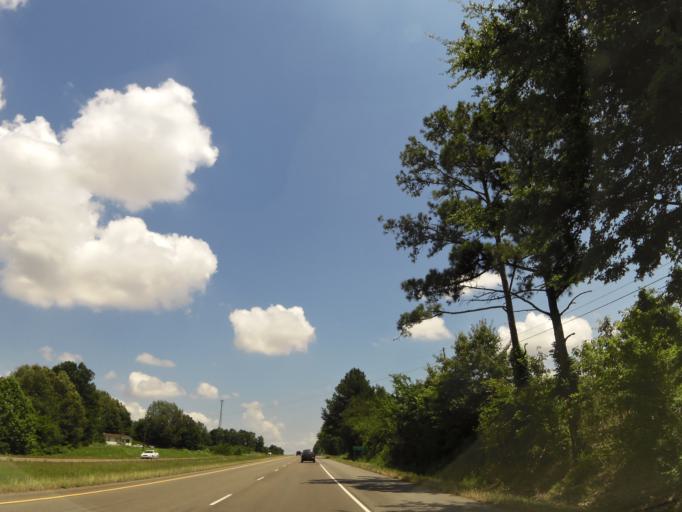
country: US
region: Tennessee
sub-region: Lauderdale County
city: Halls
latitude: 35.9135
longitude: -89.2674
